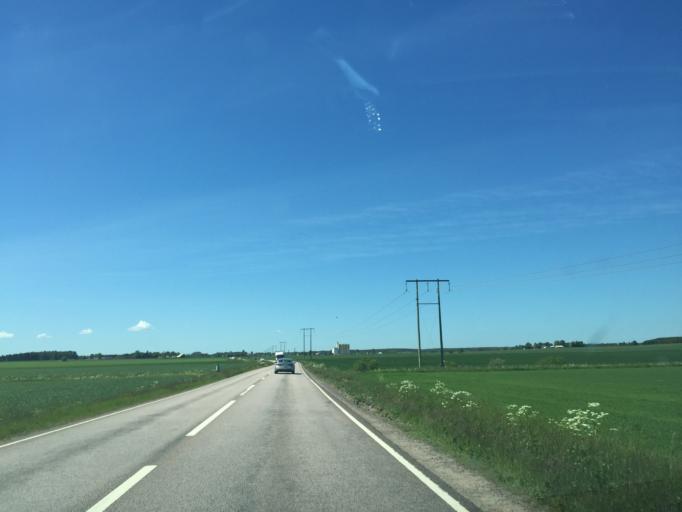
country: SE
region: OEstergoetland
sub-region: Mjolby Kommun
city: Mjolby
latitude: 58.3859
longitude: 15.1418
